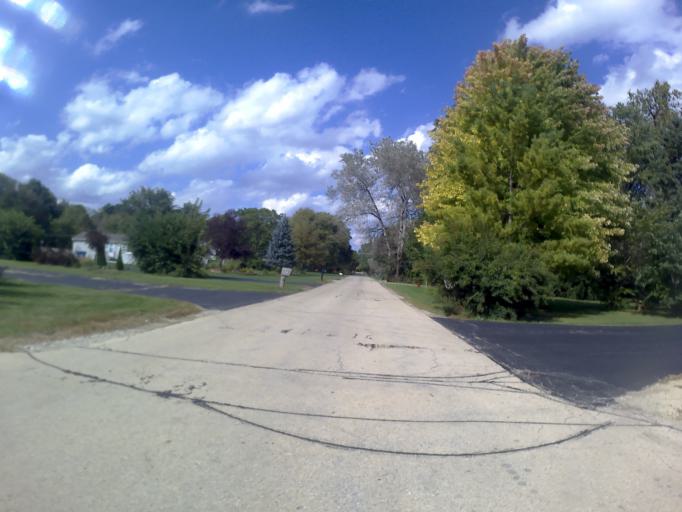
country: US
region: Illinois
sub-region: DuPage County
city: Lisle
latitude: 41.8013
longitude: -88.0824
